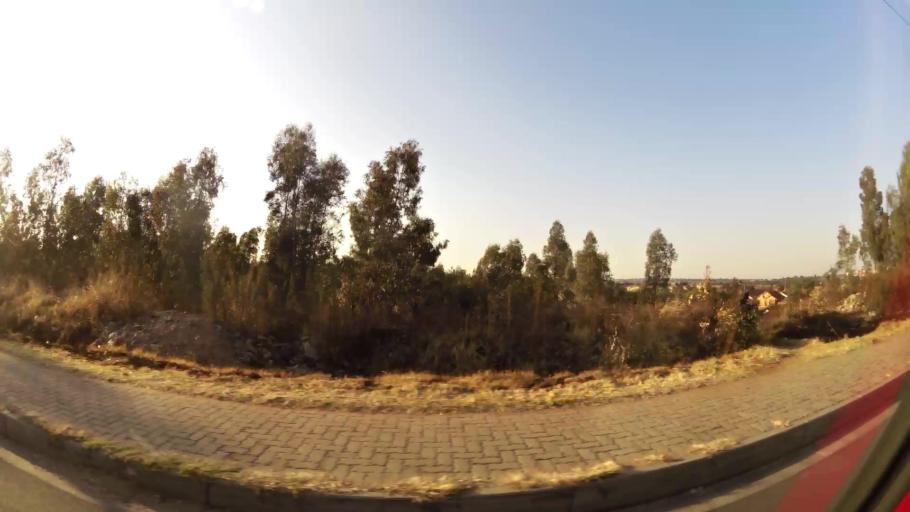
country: ZA
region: Gauteng
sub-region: City of Johannesburg Metropolitan Municipality
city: Johannesburg
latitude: -26.2137
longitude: 27.9877
